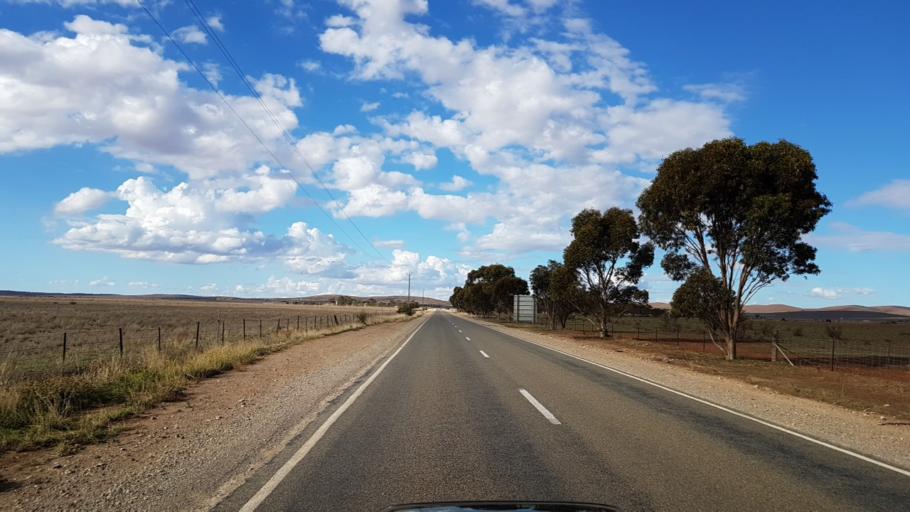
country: AU
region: South Australia
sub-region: Peterborough
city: Peterborough
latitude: -32.9699
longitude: 138.8575
